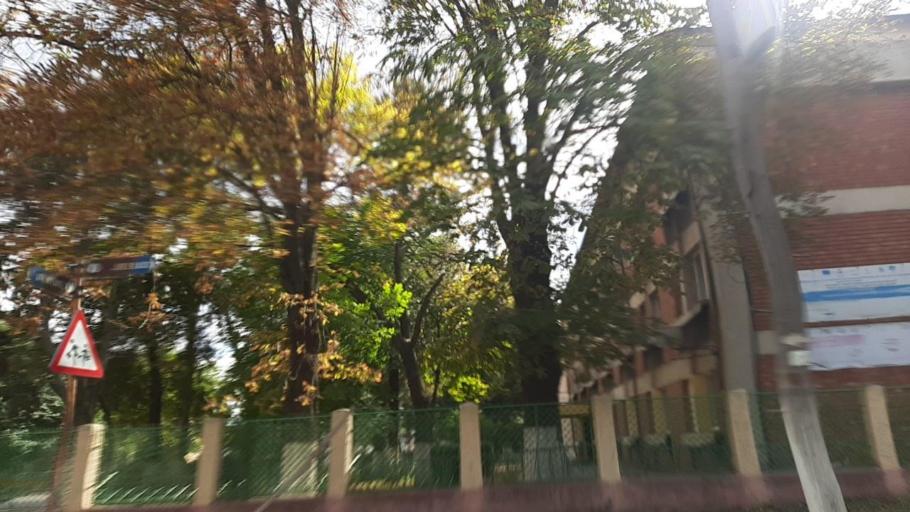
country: RO
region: Galati
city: Galati
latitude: 45.4484
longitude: 28.0341
